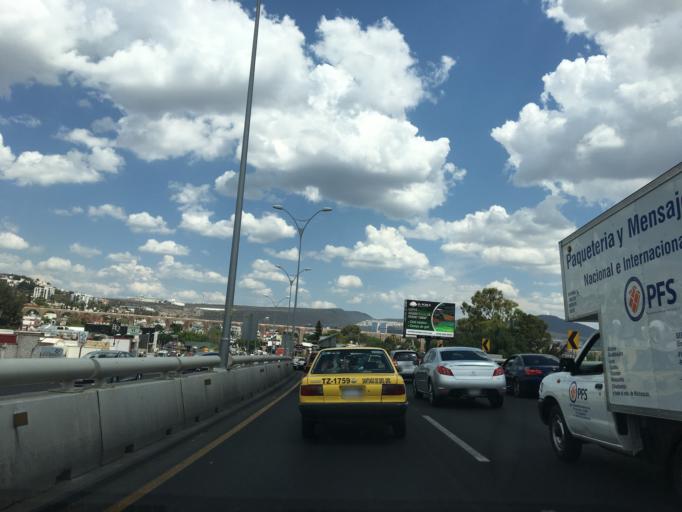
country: MX
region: Queretaro
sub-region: Queretaro
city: Santiago de Queretaro
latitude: 20.6002
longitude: -100.3758
